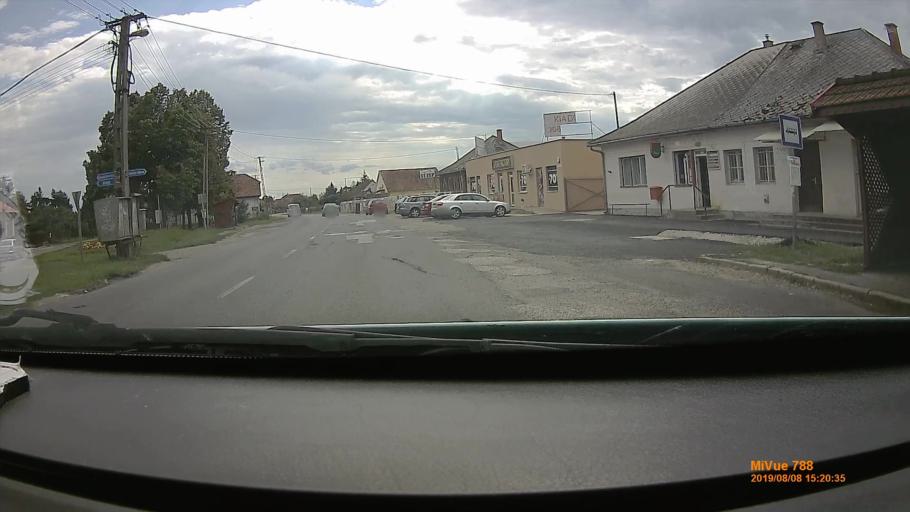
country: HU
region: Szabolcs-Szatmar-Bereg
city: Tunyogmatolcs
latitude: 47.9706
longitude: 22.4527
